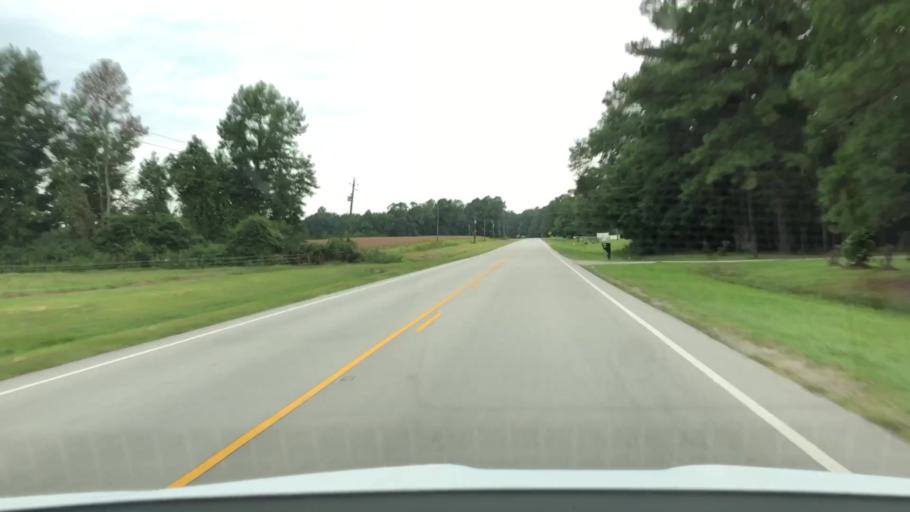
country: US
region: North Carolina
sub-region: Jones County
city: Trenton
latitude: 35.0292
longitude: -77.3114
